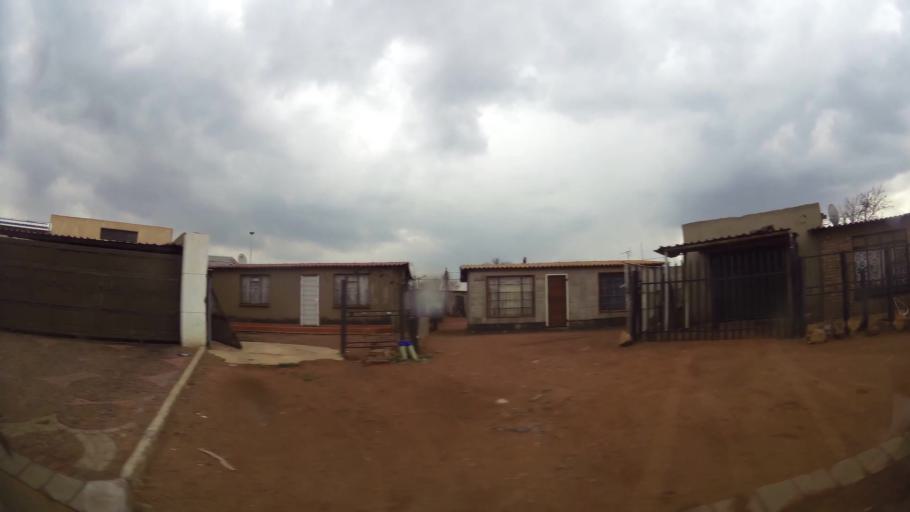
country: ZA
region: Gauteng
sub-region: Ekurhuleni Metropolitan Municipality
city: Germiston
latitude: -26.3596
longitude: 28.1565
